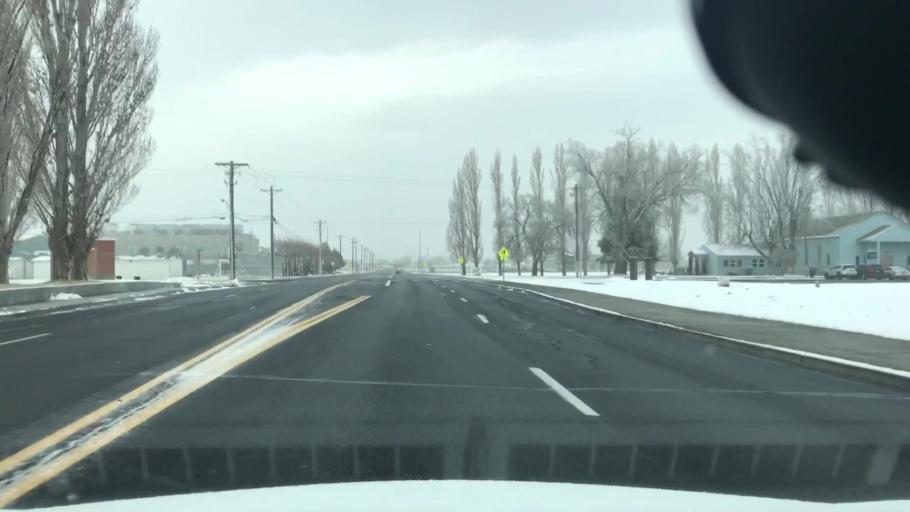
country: US
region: Washington
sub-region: Grant County
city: Moses Lake North
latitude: 47.1848
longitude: -119.3227
